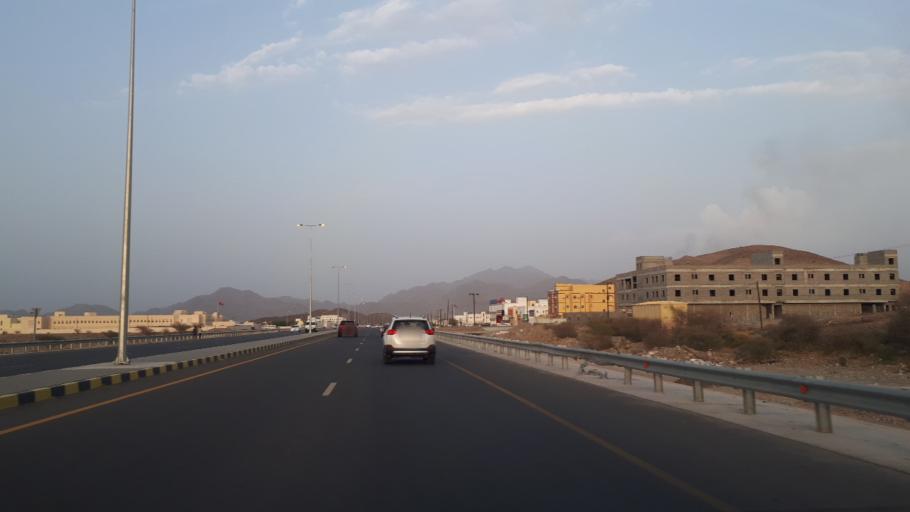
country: OM
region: Al Batinah
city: Rustaq
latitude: 23.4390
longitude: 57.4052
